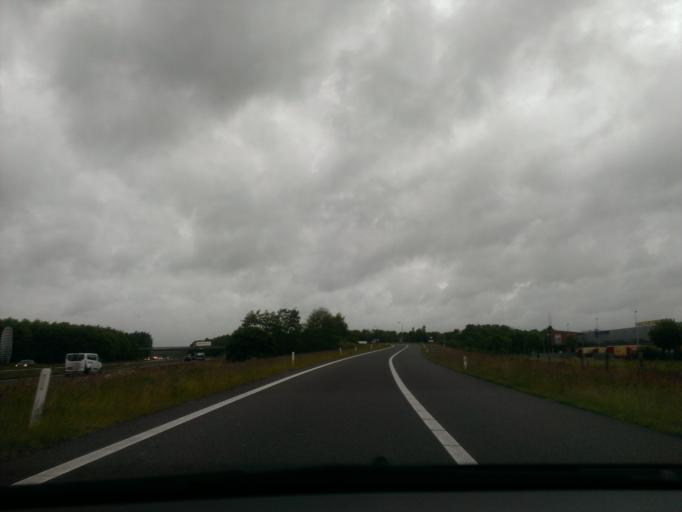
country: NL
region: Drenthe
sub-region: Gemeente Hoogeveen
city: Hoogeveen
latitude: 52.7361
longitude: 6.4658
